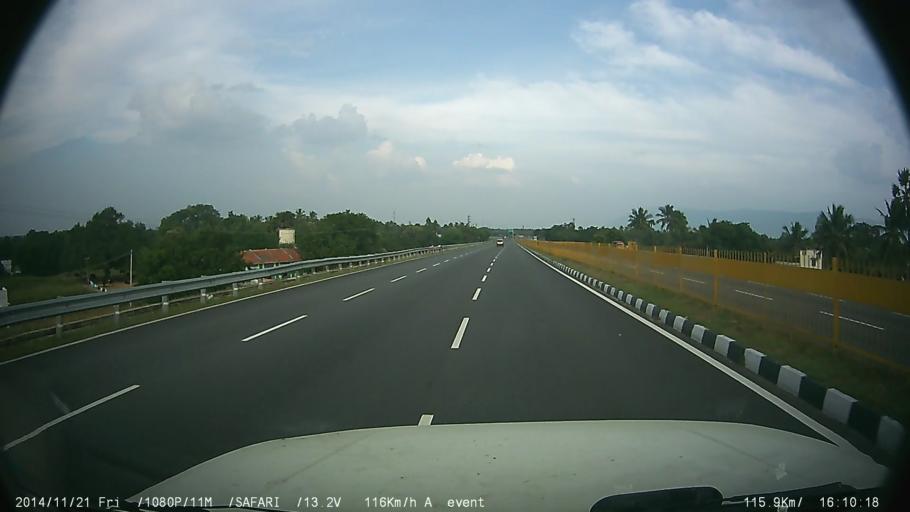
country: IN
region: Tamil Nadu
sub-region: Vellore
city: Jolarpettai
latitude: 12.5809
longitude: 78.4950
